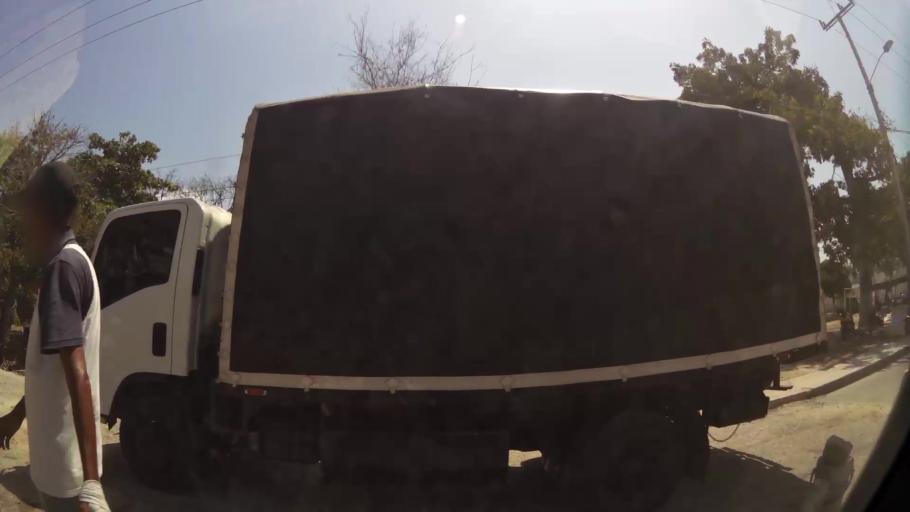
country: CO
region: Bolivar
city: Cartagena
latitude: 10.4025
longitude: -75.4870
